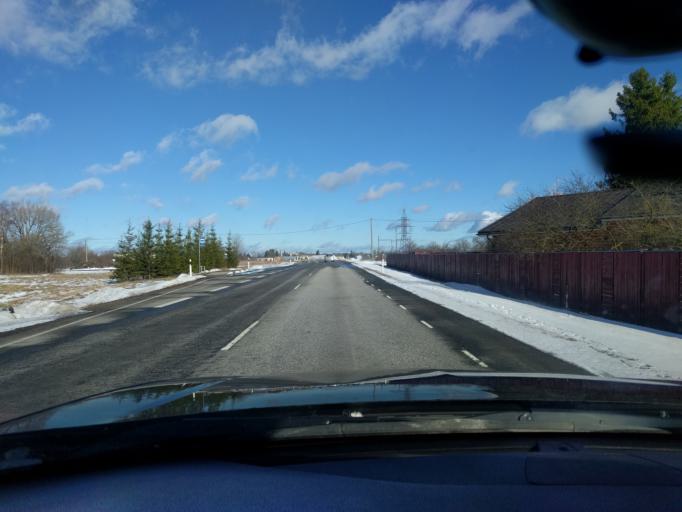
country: EE
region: Harju
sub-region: Raasiku vald
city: Raasiku
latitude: 59.3694
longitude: 25.1919
